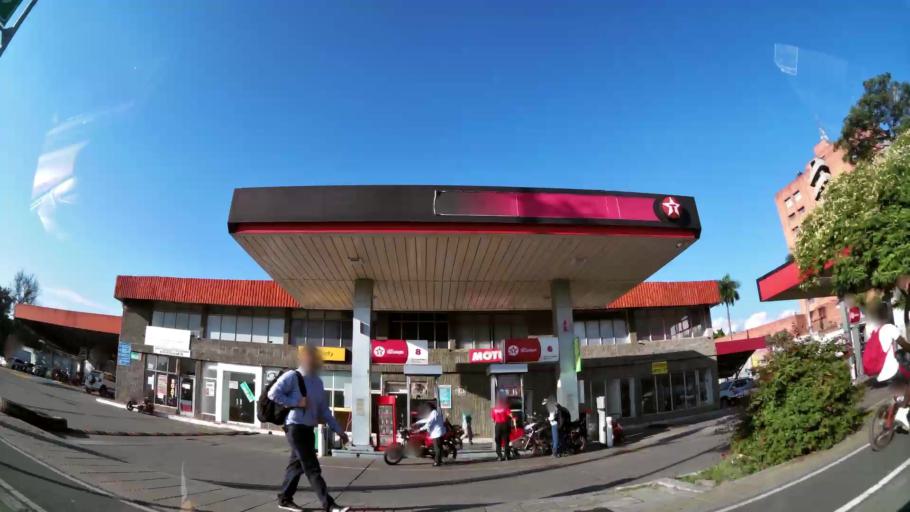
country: CO
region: Valle del Cauca
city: Cali
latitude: 3.4352
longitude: -76.5149
